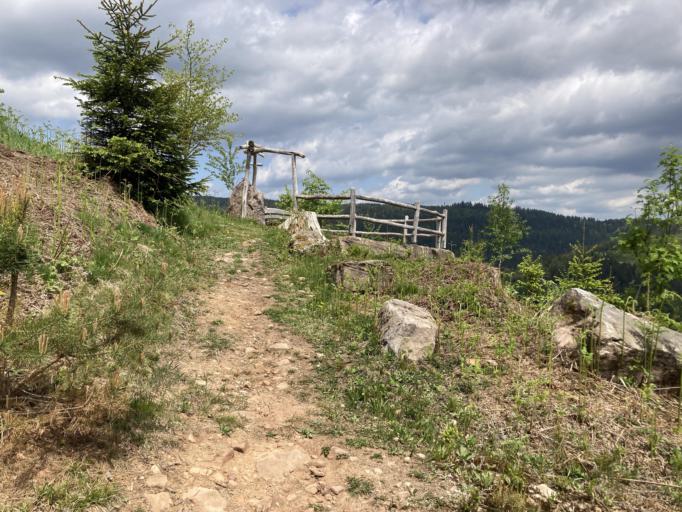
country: DE
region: Baden-Wuerttemberg
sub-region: Karlsruhe Region
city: Baiersbronn
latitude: 48.5260
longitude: 8.2980
